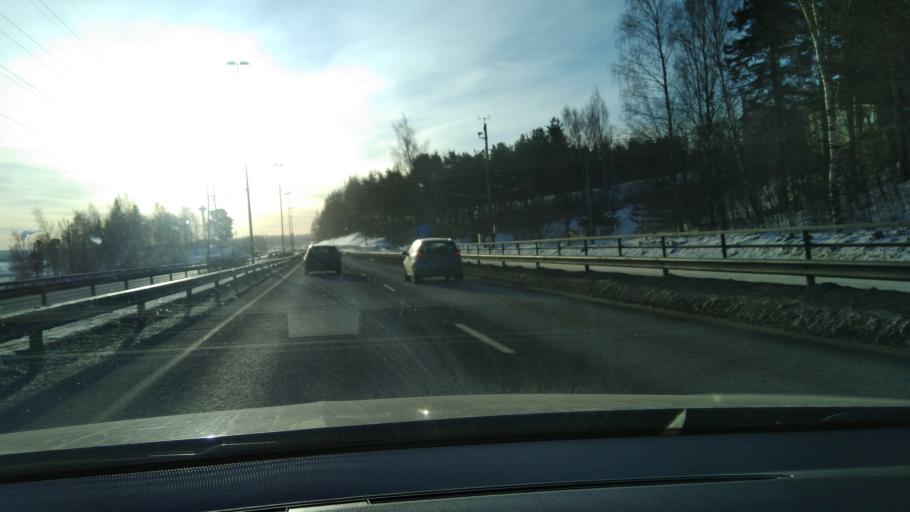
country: FI
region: Pirkanmaa
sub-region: Tampere
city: Pirkkala
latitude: 61.5086
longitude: 23.6967
